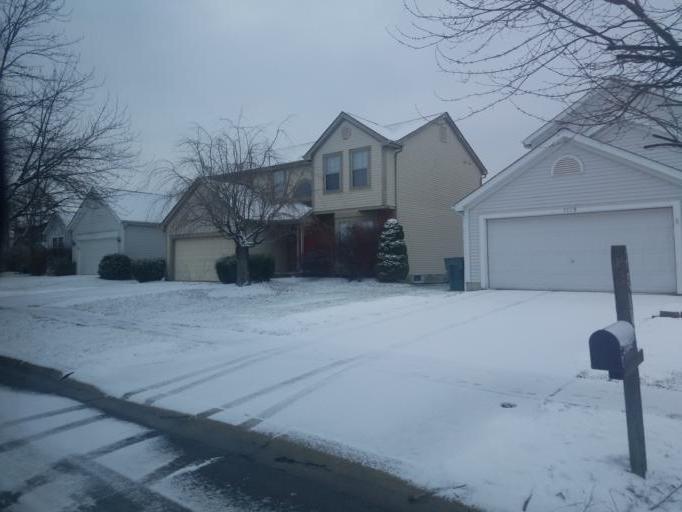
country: US
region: Ohio
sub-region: Franklin County
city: Reynoldsburg
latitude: 39.9962
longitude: -82.7902
